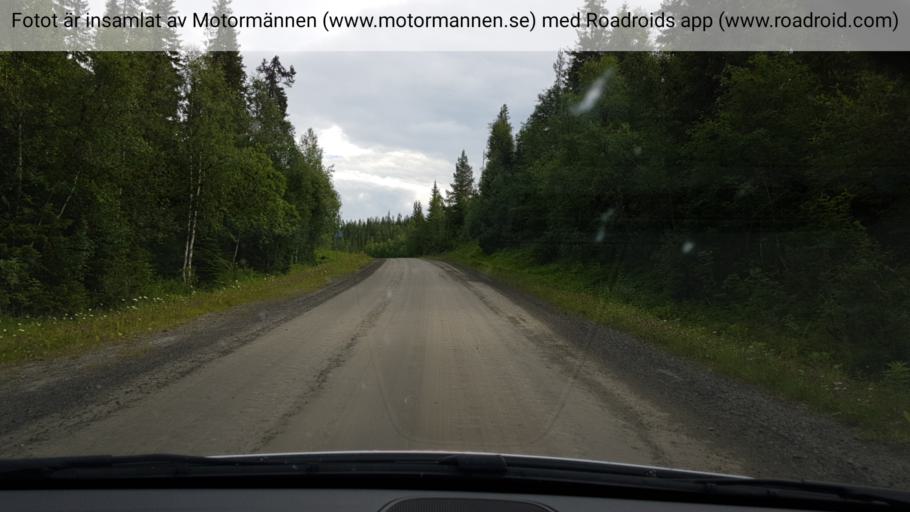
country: SE
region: Jaemtland
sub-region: Are Kommun
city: Are
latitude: 63.7189
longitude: 12.6086
